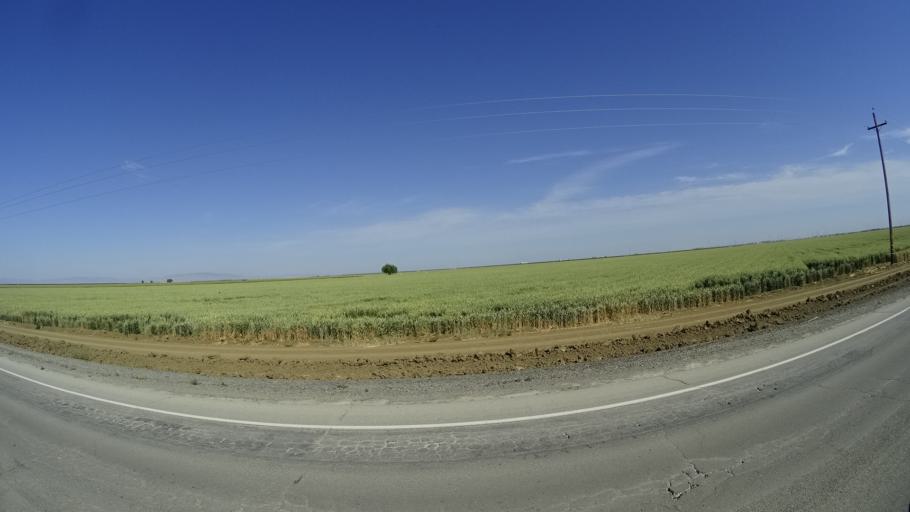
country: US
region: California
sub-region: Kings County
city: Lemoore Station
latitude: 36.2087
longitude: -119.9206
